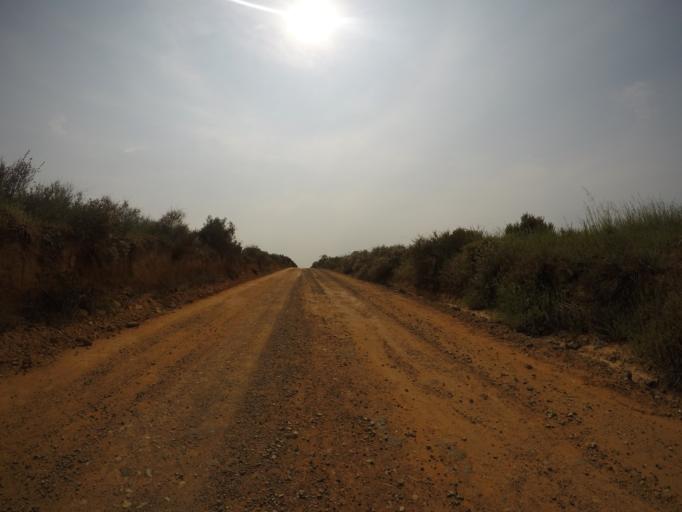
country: ZA
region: Western Cape
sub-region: West Coast District Municipality
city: Malmesbury
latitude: -33.4484
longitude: 18.7465
